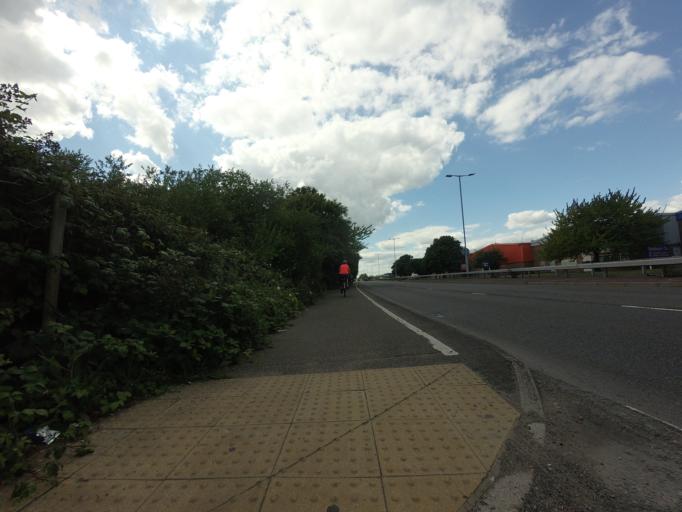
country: GB
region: England
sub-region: East Sussex
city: Eastbourne
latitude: 50.7890
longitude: 0.3000
